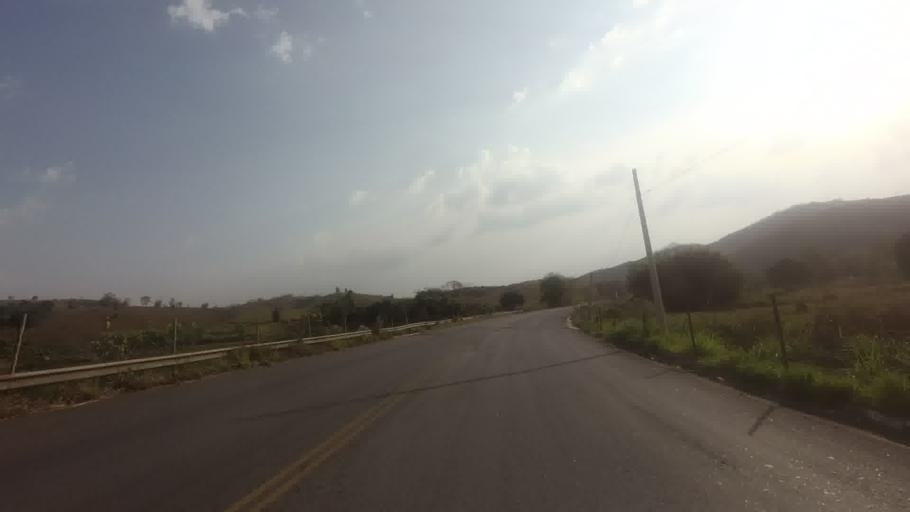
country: BR
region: Rio de Janeiro
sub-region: Itaperuna
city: Itaperuna
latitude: -21.3830
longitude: -41.9582
